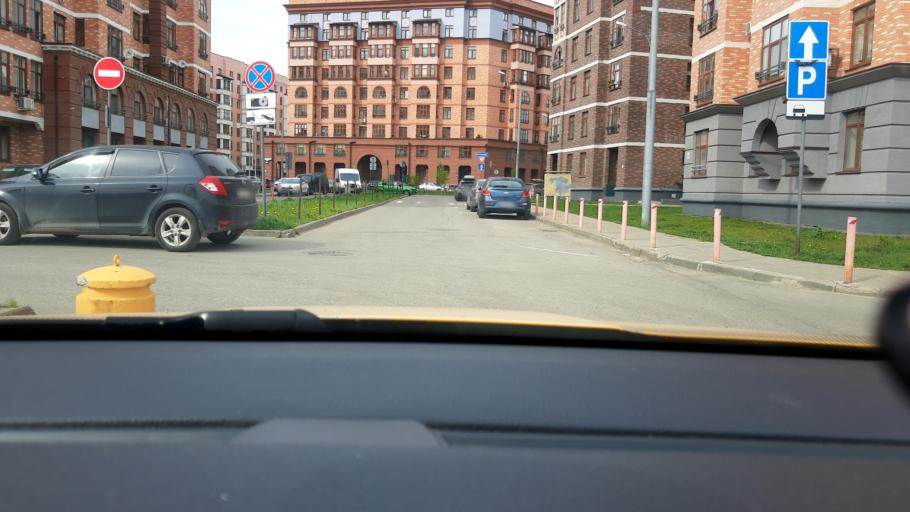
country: RU
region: Moskovskaya
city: Opalikha
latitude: 55.8836
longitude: 37.2693
